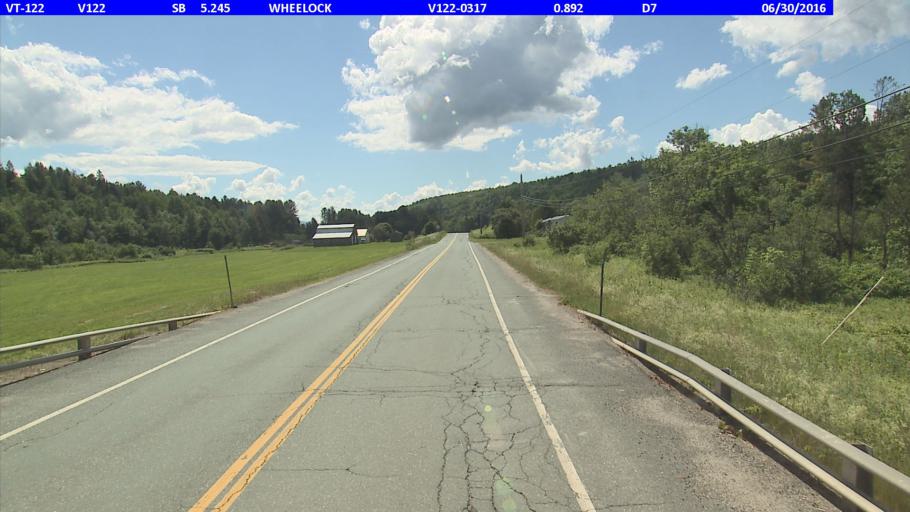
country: US
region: Vermont
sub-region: Caledonia County
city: Lyndonville
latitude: 44.5856
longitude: -72.0795
